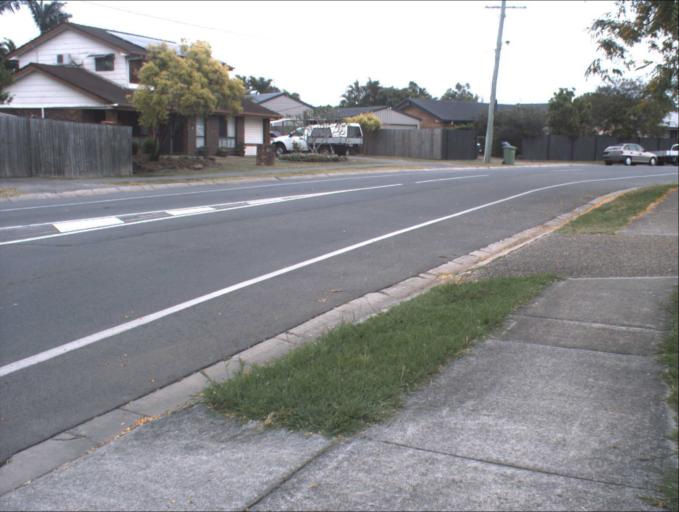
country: AU
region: Queensland
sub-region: Logan
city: Beenleigh
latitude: -27.6817
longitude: 153.1800
